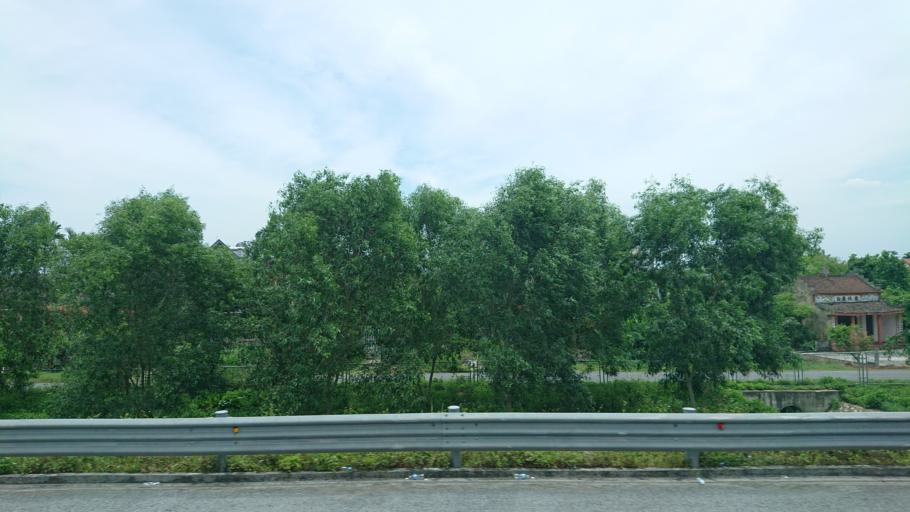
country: VN
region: Hai Phong
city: Nui Doi
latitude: 20.7680
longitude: 106.6360
